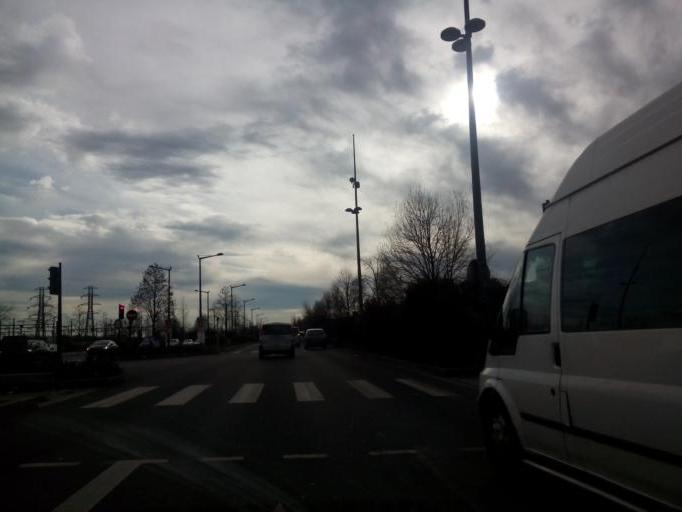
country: FR
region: Rhone-Alpes
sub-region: Departement du Rhone
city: Saint-Fons
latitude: 45.7231
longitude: 4.8422
